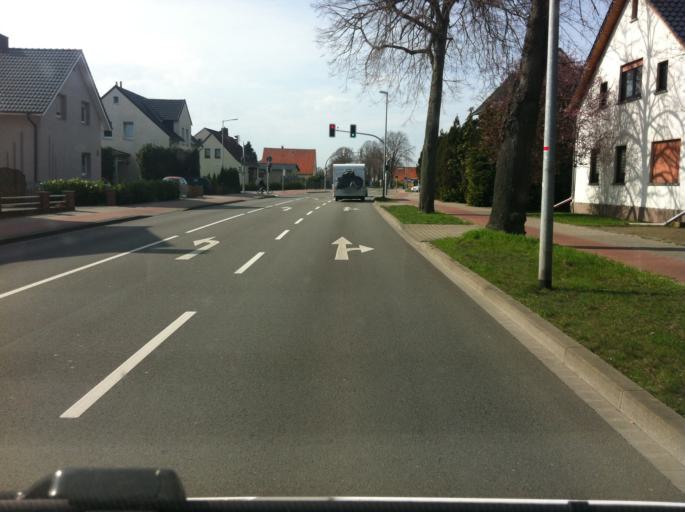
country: DE
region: North Rhine-Westphalia
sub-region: Regierungsbezirk Detmold
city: Minden
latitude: 52.2922
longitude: 8.8810
